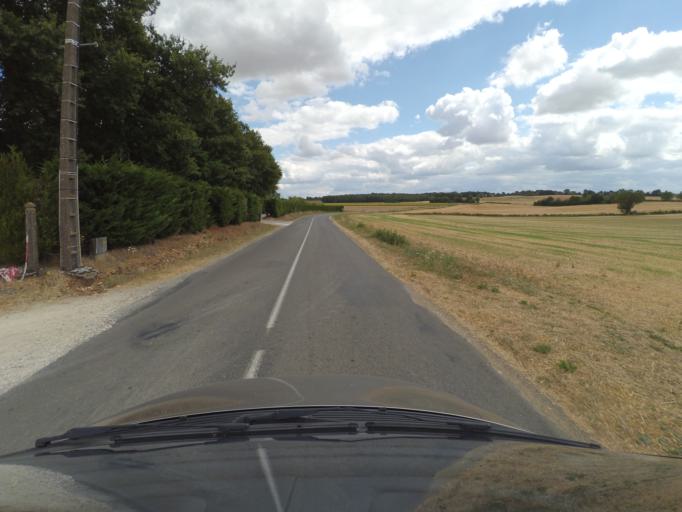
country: FR
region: Poitou-Charentes
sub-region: Departement de la Vienne
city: Saint-Savin
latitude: 46.5450
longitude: 0.9810
